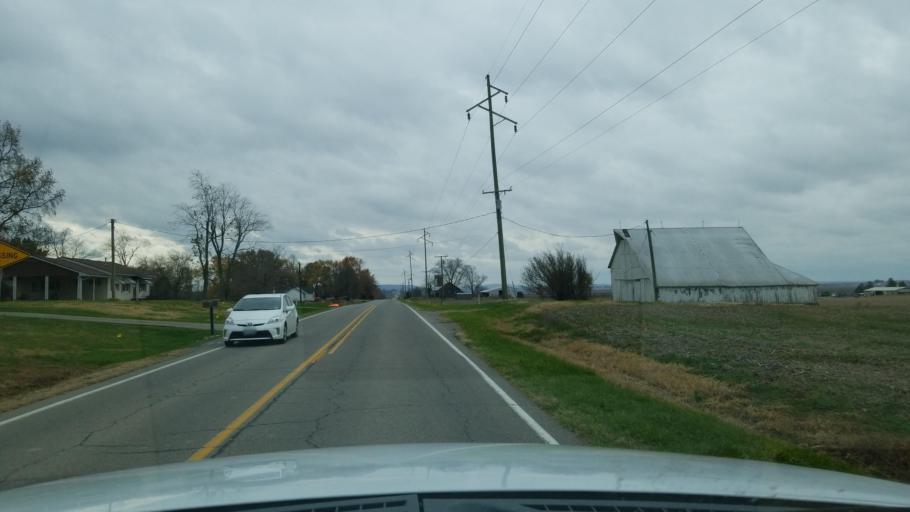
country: US
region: Illinois
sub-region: Saline County
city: Eldorado
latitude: 37.7950
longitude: -88.4382
